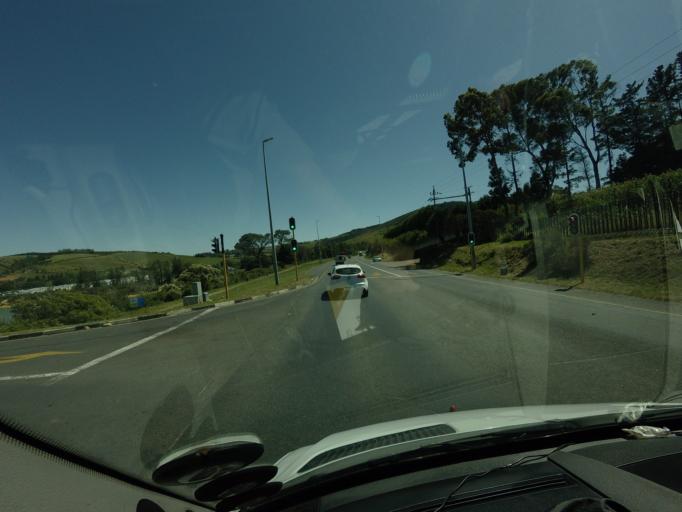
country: ZA
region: Western Cape
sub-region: Cape Winelands District Municipality
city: Stellenbosch
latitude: -33.9017
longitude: 18.8588
